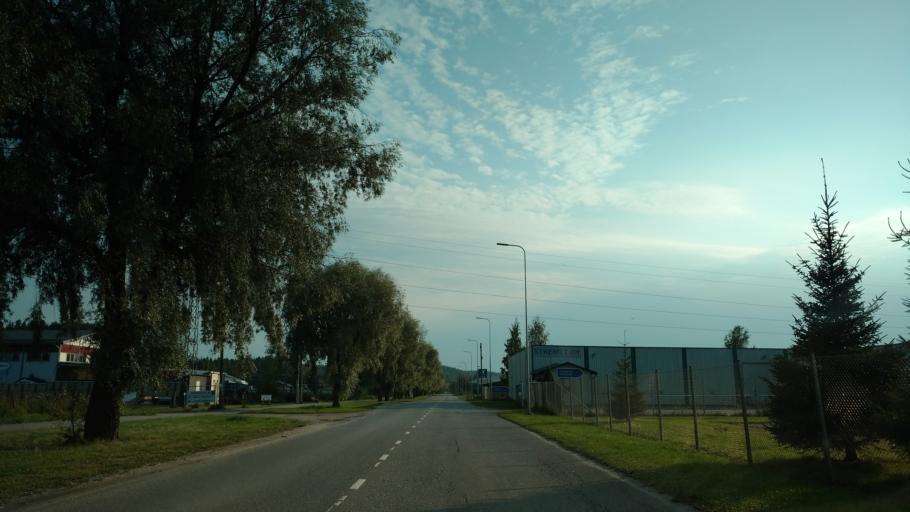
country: FI
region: Varsinais-Suomi
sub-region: Salo
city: Salo
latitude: 60.3756
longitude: 23.1091
